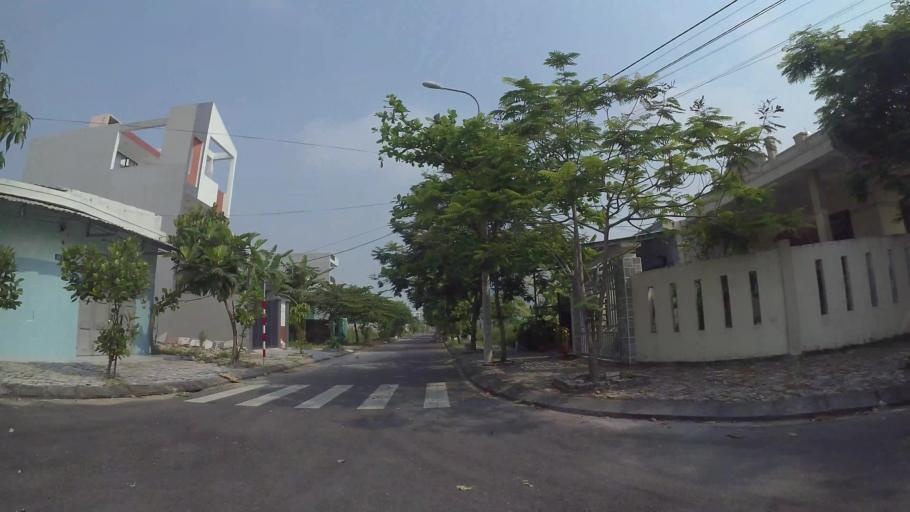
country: VN
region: Da Nang
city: Cam Le
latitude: 15.9931
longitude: 108.2147
